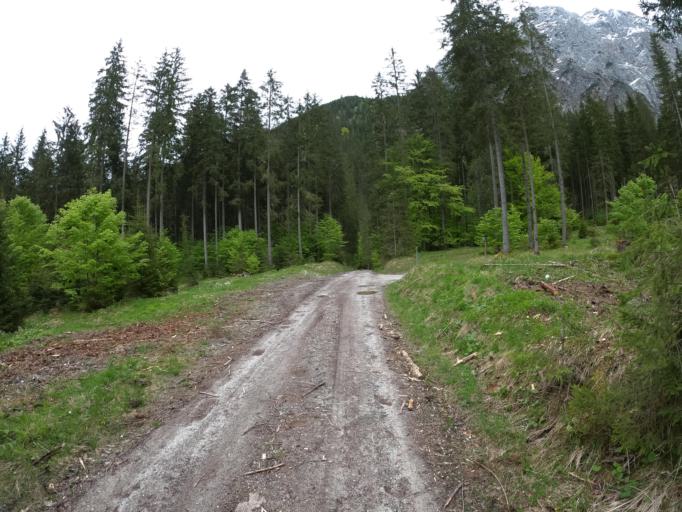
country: AT
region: Salzburg
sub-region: Politischer Bezirk Sankt Johann im Pongau
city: Werfen
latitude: 47.4668
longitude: 13.0808
